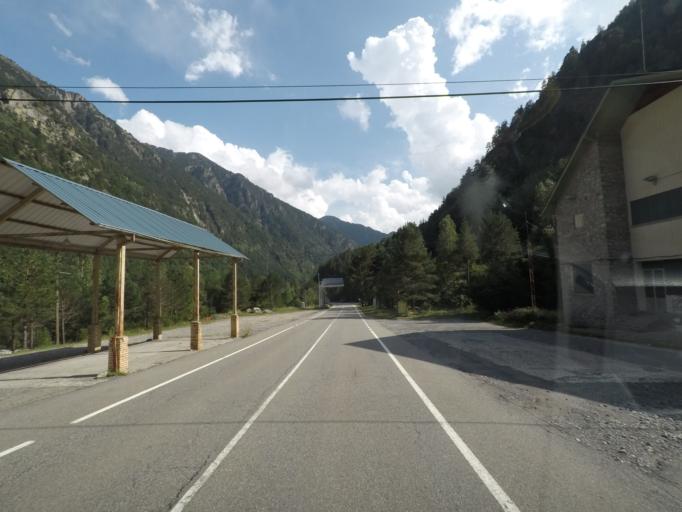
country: ES
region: Aragon
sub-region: Provincia de Huesca
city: Bielsa
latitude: 42.6902
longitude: 0.2071
